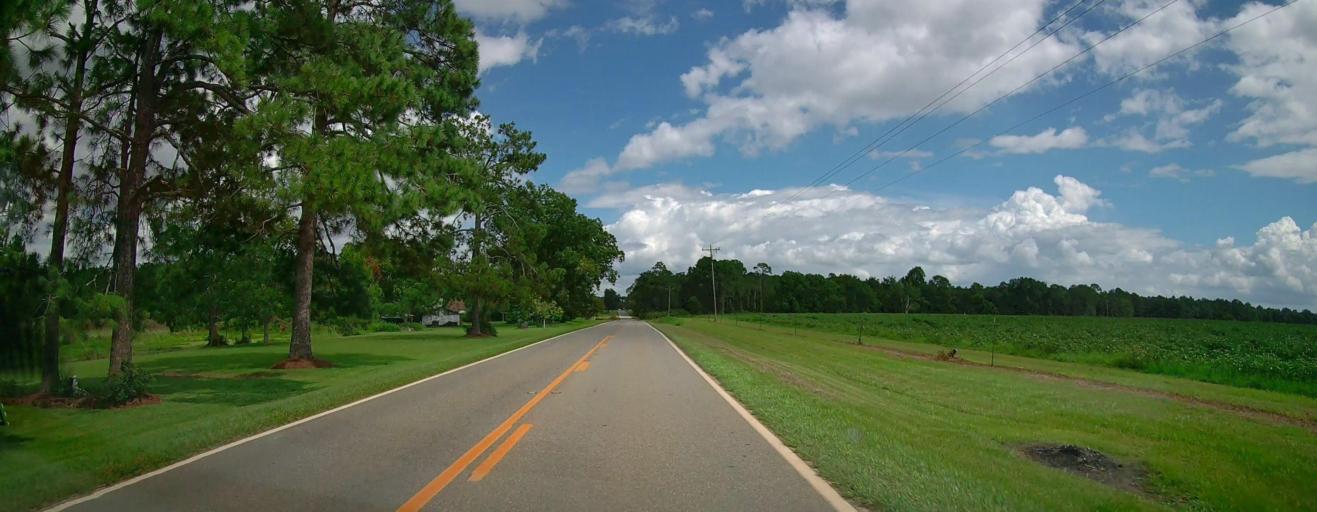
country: US
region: Georgia
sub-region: Ben Hill County
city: Fitzgerald
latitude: 31.6831
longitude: -83.2054
